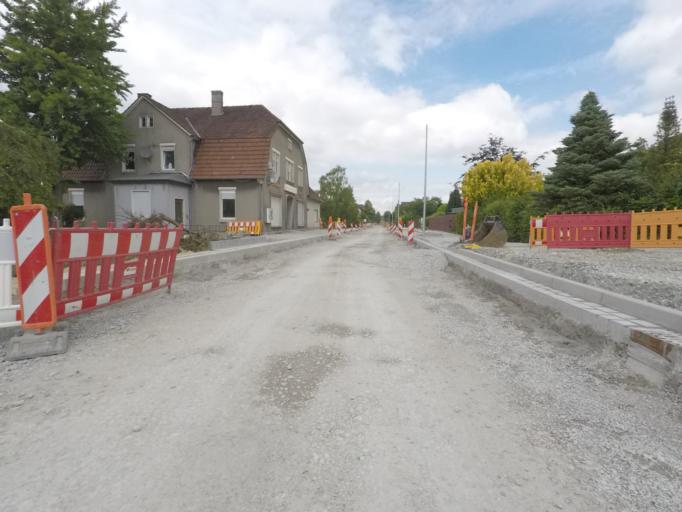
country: DE
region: Lower Saxony
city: Neuenkirchen
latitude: 52.1088
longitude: 8.3691
